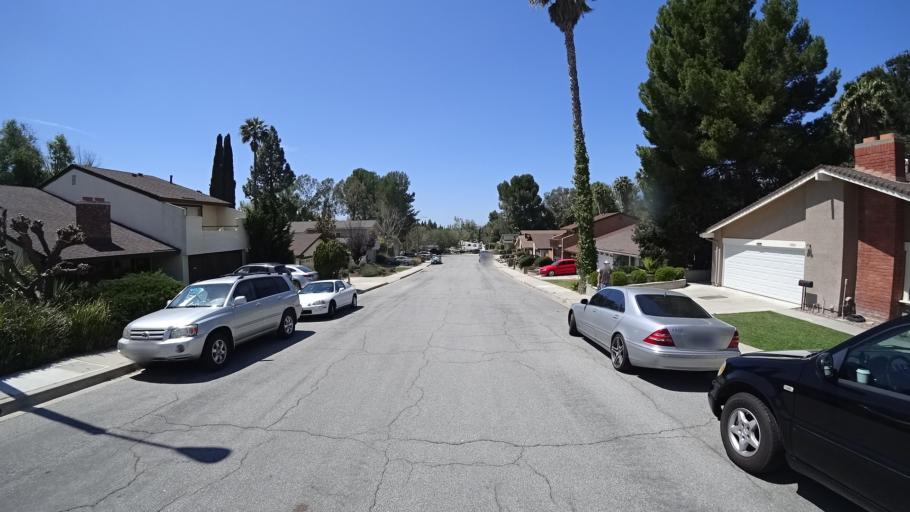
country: US
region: California
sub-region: Ventura County
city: Thousand Oaks
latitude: 34.2132
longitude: -118.8424
